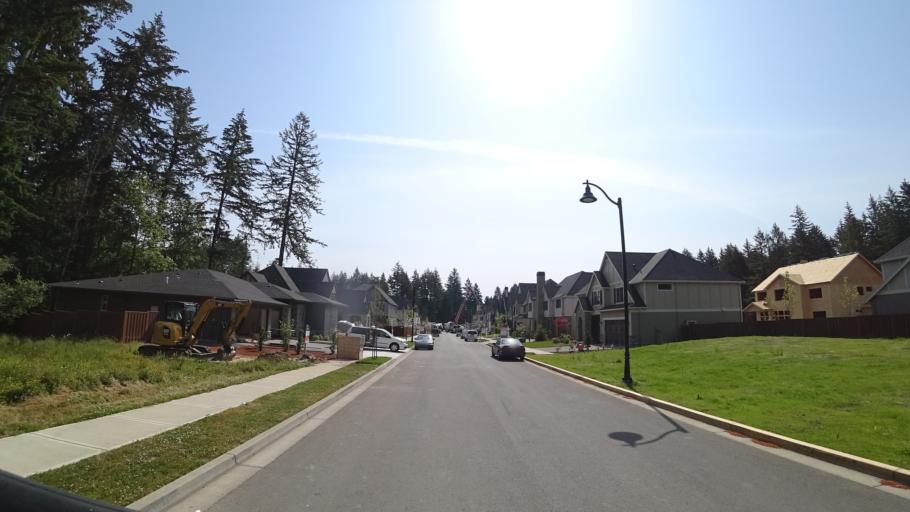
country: US
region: Oregon
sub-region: Clackamas County
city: Happy Valley
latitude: 45.4513
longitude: -122.5063
